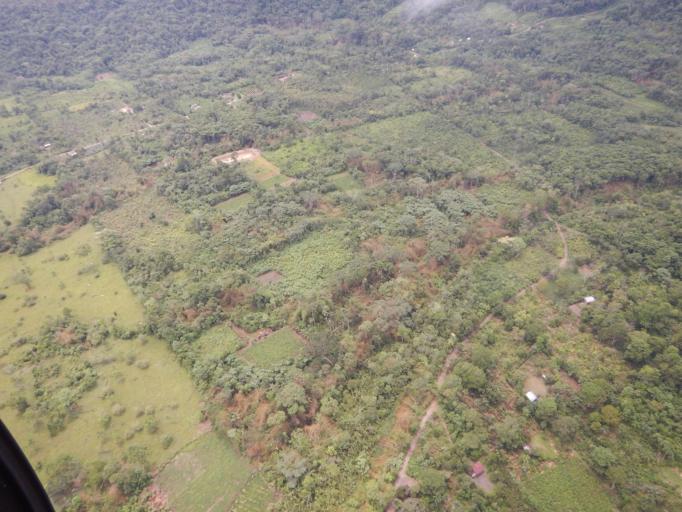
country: BO
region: Cochabamba
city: Chimore
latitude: -17.1007
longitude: -65.1946
